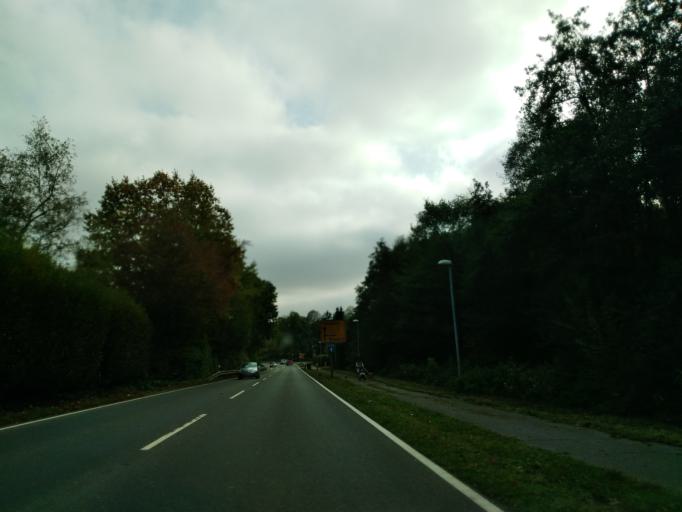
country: DE
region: North Rhine-Westphalia
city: Sankt Augustin
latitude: 50.7506
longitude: 7.2202
